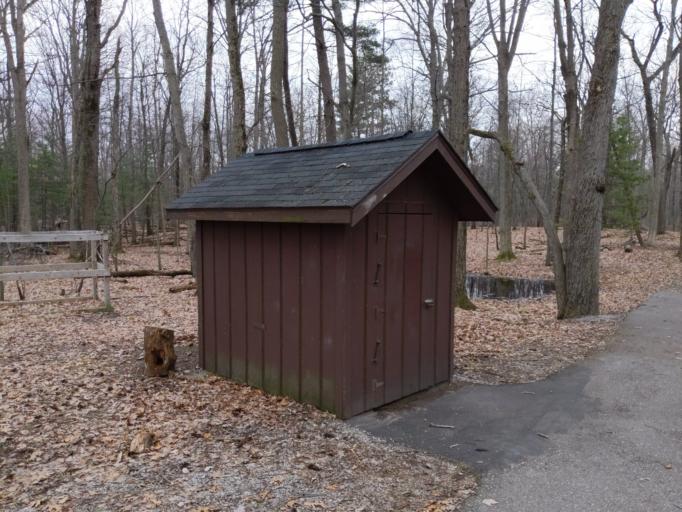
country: US
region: Michigan
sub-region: Bay County
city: Bay City
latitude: 43.6783
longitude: -83.9242
